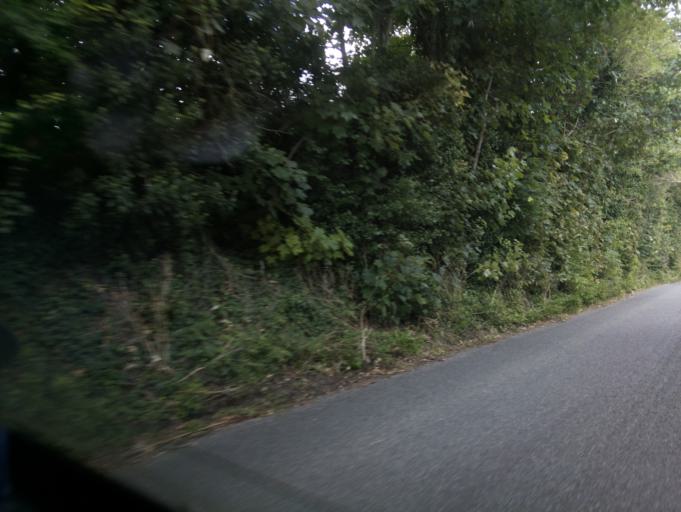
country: GB
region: England
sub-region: Wiltshire
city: Biddestone
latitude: 51.4706
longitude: -2.2370
